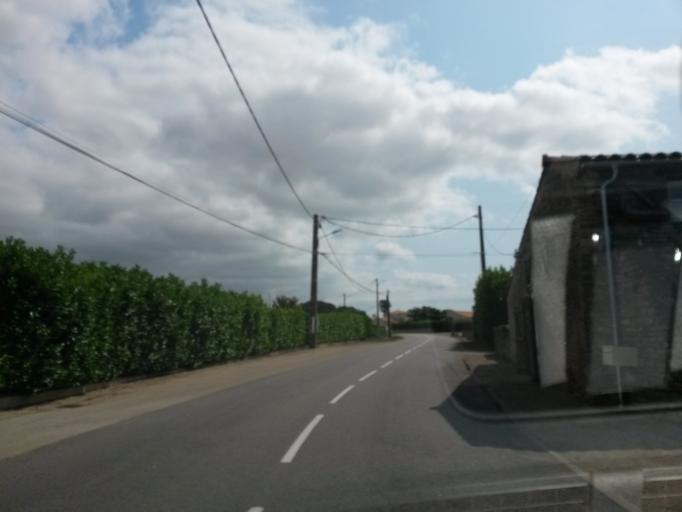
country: FR
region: Pays de la Loire
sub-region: Departement de la Vendee
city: Jard-sur-Mer
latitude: 46.4350
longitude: -1.5815
